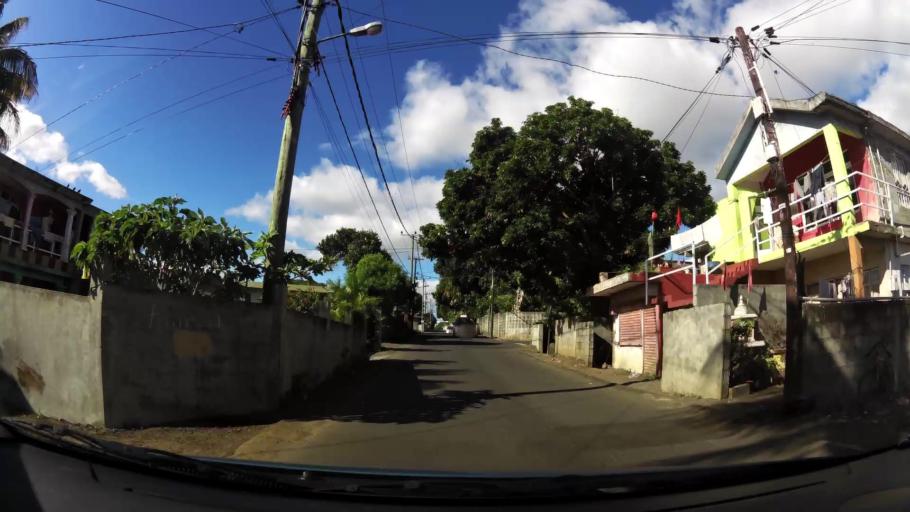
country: MU
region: Plaines Wilhems
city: Vacoas
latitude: -20.2842
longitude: 57.4884
